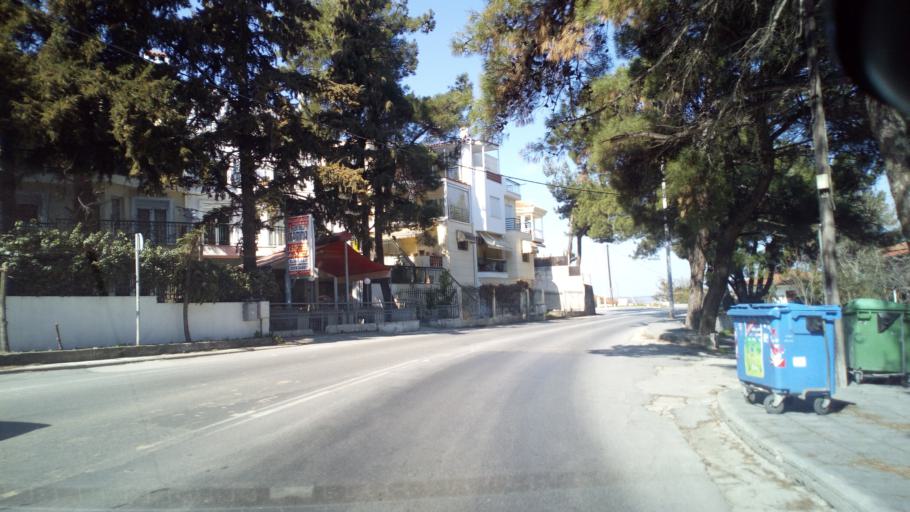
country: GR
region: Central Macedonia
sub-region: Nomos Thessalonikis
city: Panorama
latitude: 40.5922
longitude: 23.0429
